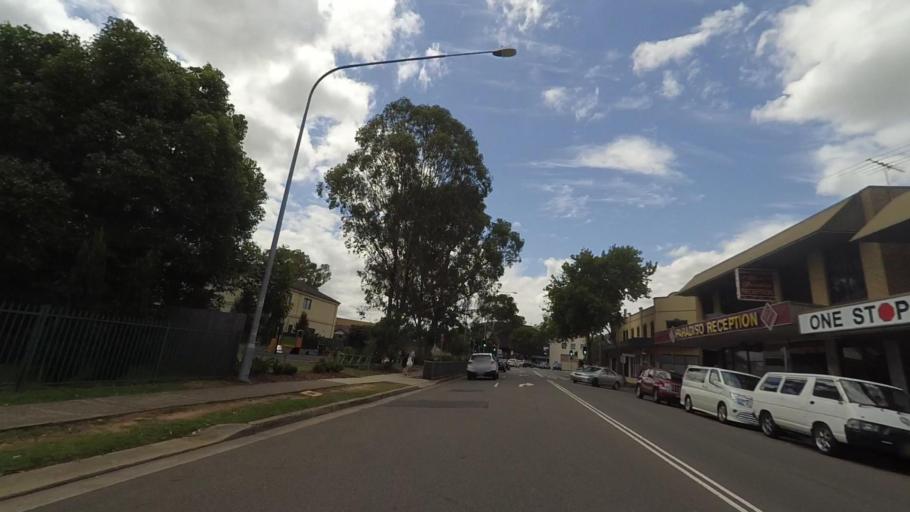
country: AU
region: New South Wales
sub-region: Fairfield
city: Fairfield Heights
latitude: -33.8699
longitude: 150.9533
